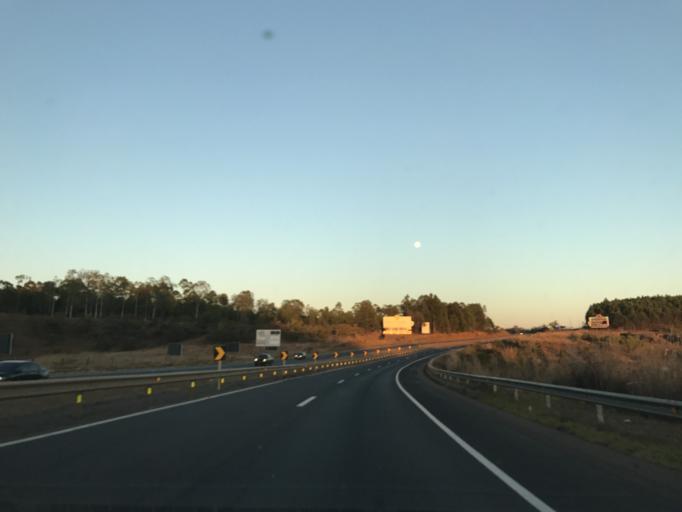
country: BR
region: Goias
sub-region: Abadiania
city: Abadiania
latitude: -16.1908
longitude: -48.6739
